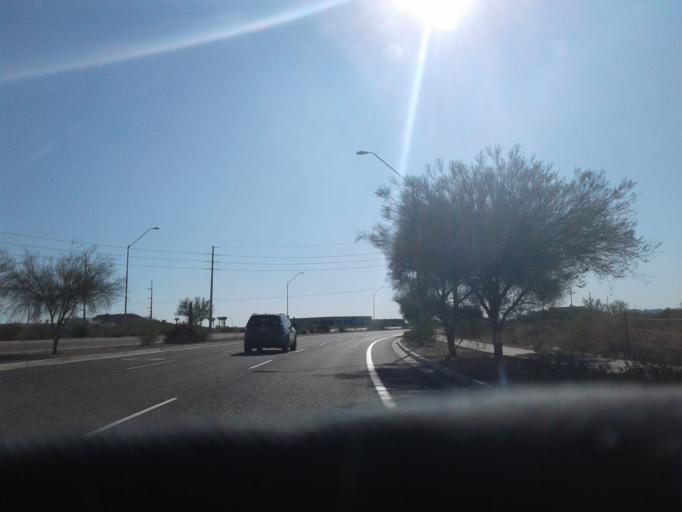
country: US
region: Arizona
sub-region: Maricopa County
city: Cave Creek
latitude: 33.6849
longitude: -112.0537
